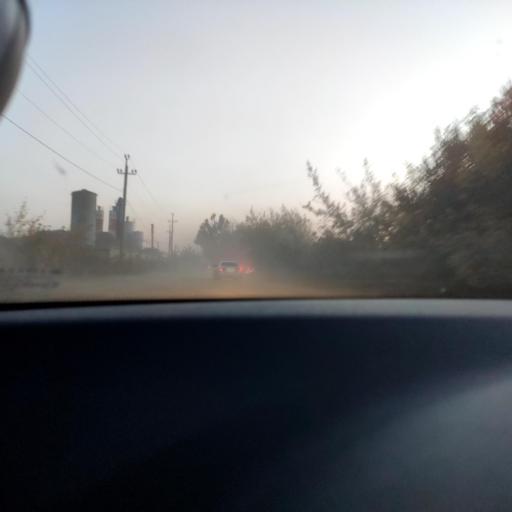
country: RU
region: Samara
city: Novosemeykino
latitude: 53.3575
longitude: 50.3528
